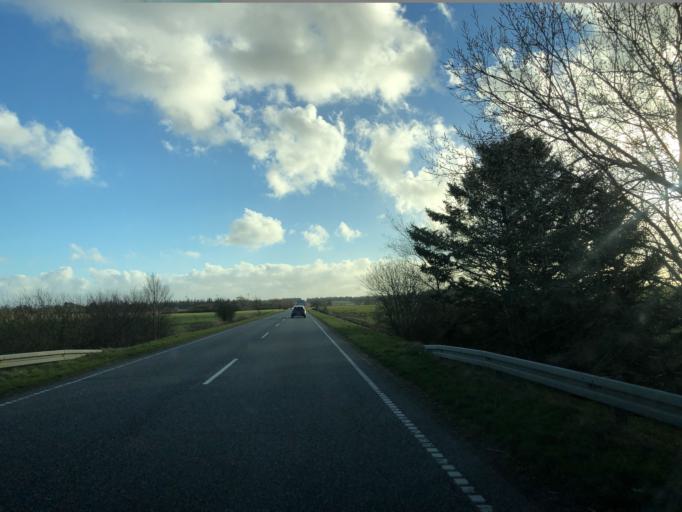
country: DK
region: Central Jutland
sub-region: Herning Kommune
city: Vildbjerg
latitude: 56.1956
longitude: 8.7165
